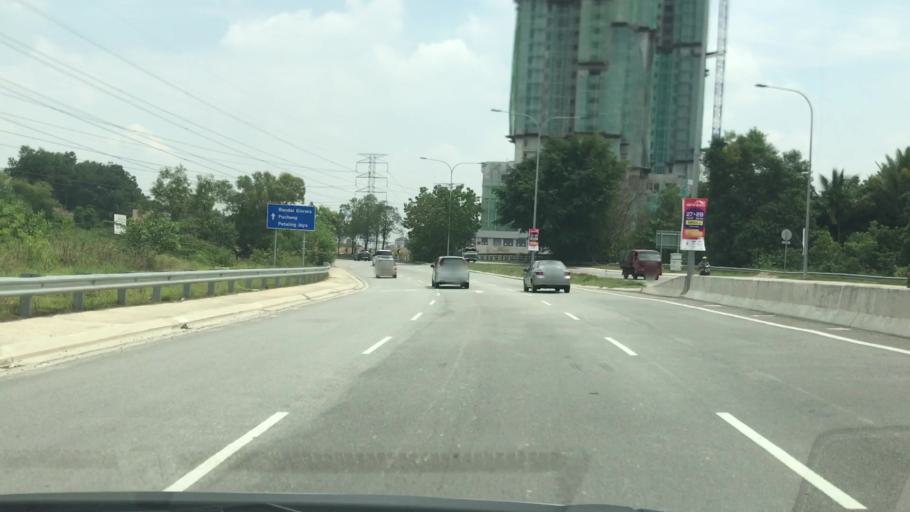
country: MY
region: Selangor
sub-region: Petaling
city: Petaling Jaya
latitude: 3.0545
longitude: 101.6675
